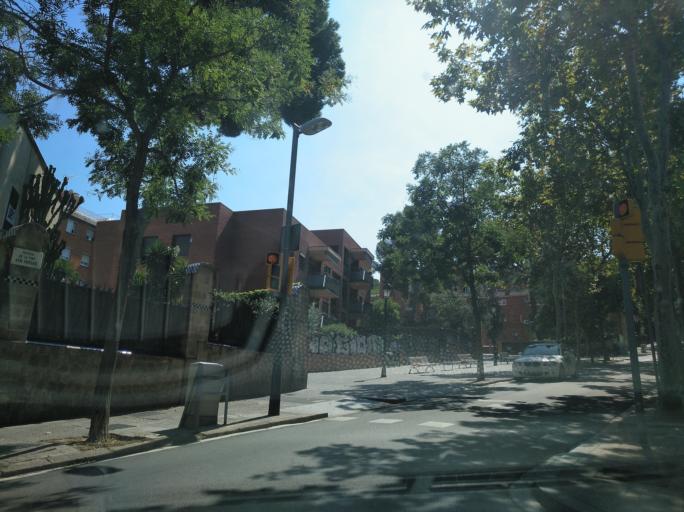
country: ES
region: Catalonia
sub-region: Provincia de Barcelona
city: Horta-Guinardo
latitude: 41.4243
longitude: 2.1654
